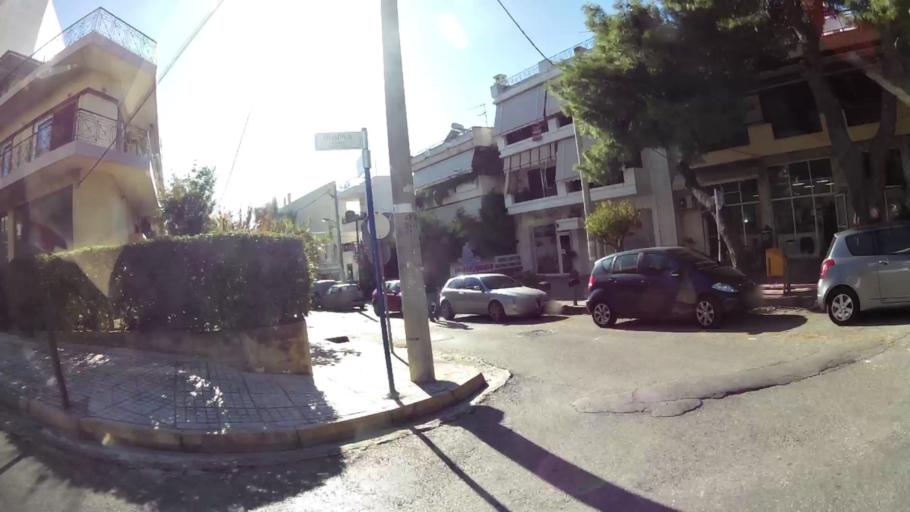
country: GR
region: Attica
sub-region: Nomarchia Athinas
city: Nea Erythraia
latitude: 38.0921
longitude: 23.8195
